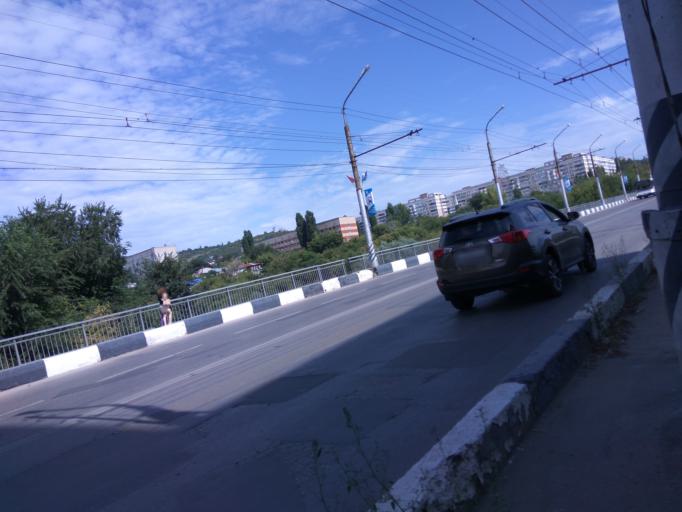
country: RU
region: Saratov
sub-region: Saratovskiy Rayon
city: Saratov
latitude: 51.5306
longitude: 46.0563
